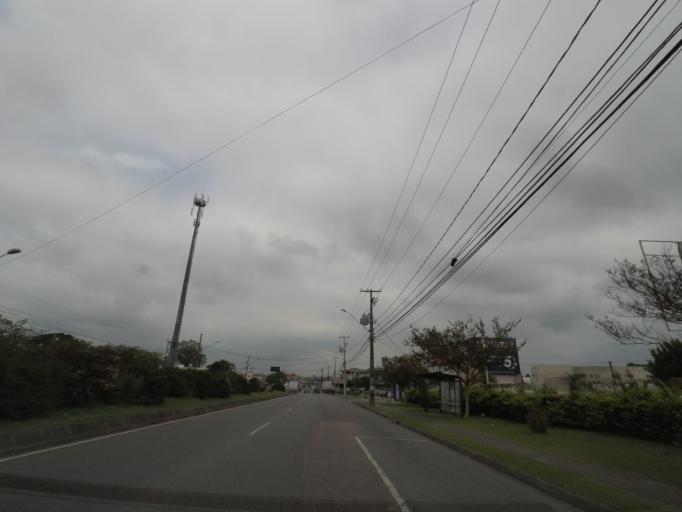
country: BR
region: Parana
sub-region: Curitiba
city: Curitiba
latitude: -25.5106
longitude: -49.3317
